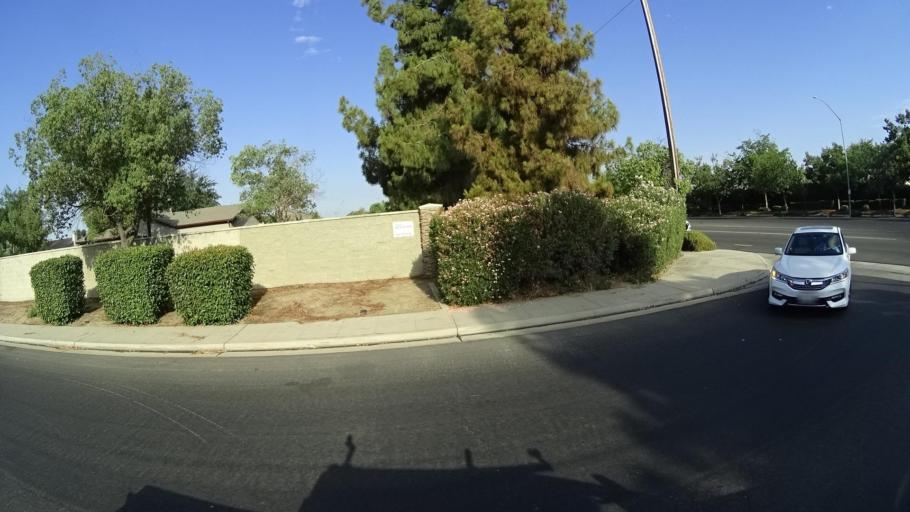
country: US
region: California
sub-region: Fresno County
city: Sunnyside
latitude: 36.7146
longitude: -119.6983
